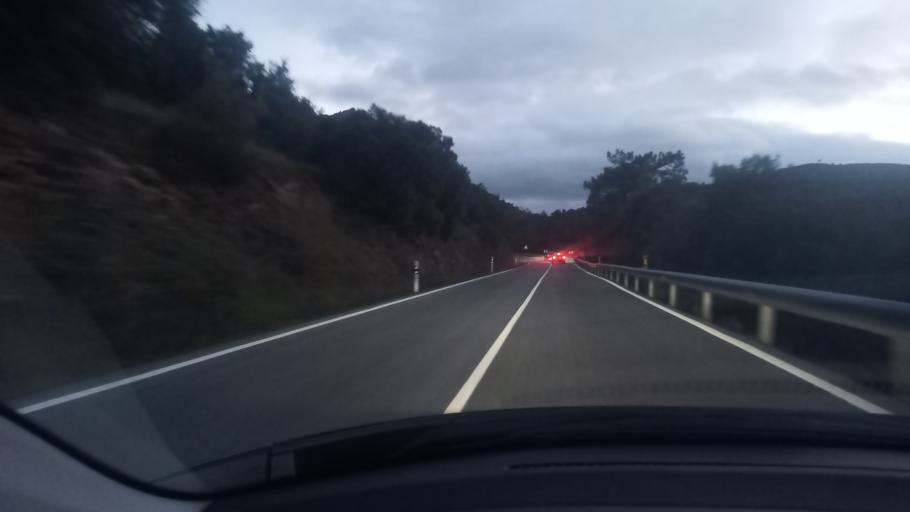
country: ES
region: Madrid
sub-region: Provincia de Madrid
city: Robledo de Chavela
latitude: 40.4674
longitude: -4.2615
